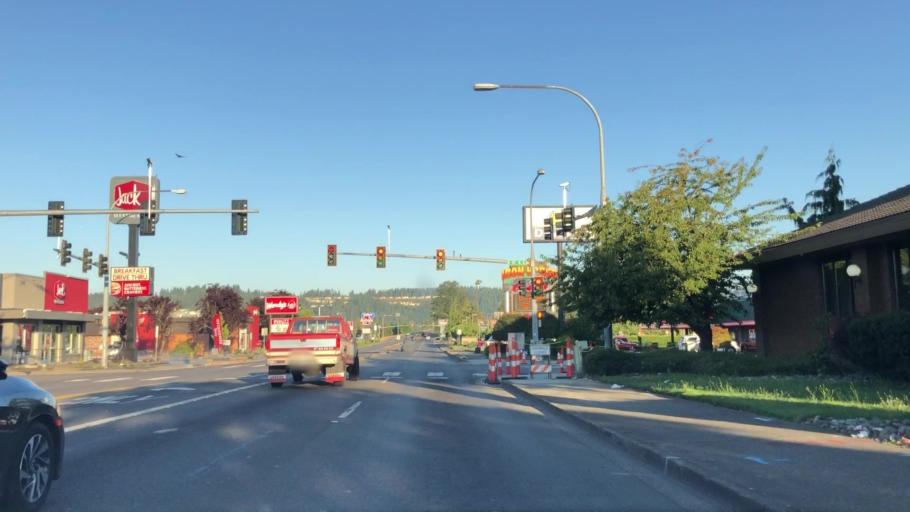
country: US
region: Washington
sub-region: King County
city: Auburn
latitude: 47.3210
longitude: -122.2244
